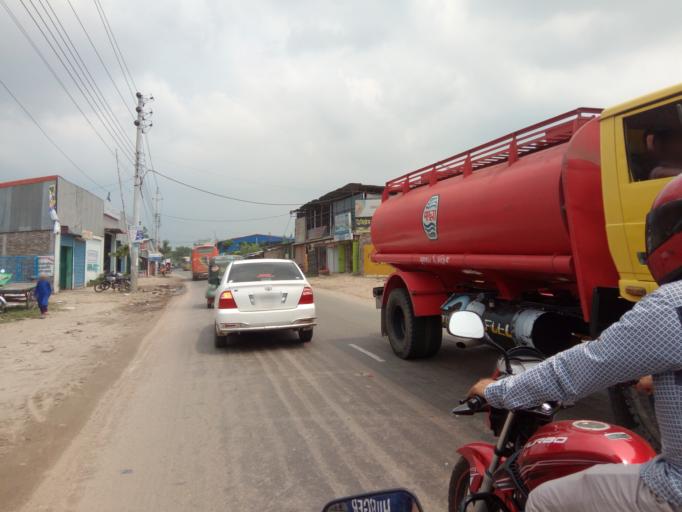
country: BD
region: Dhaka
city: Paltan
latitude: 23.7562
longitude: 90.4486
